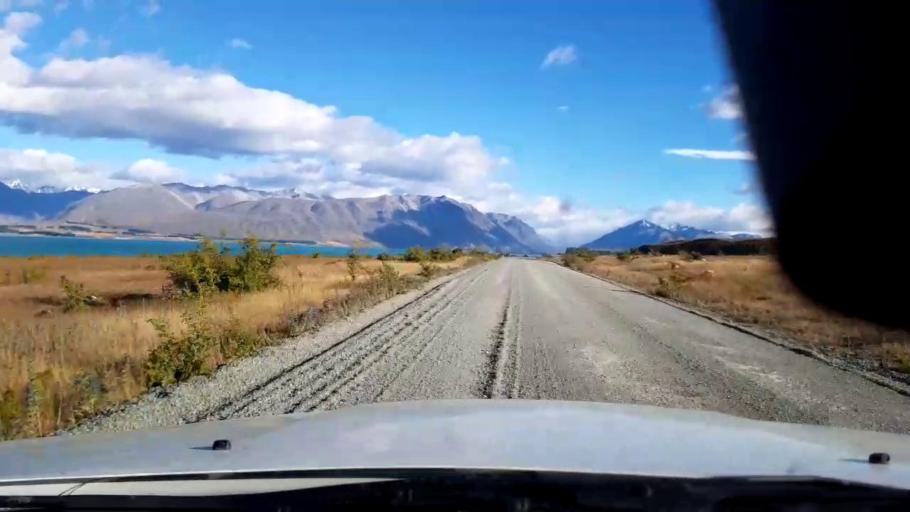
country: NZ
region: Canterbury
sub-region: Timaru District
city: Pleasant Point
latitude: -43.9160
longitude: 170.5580
